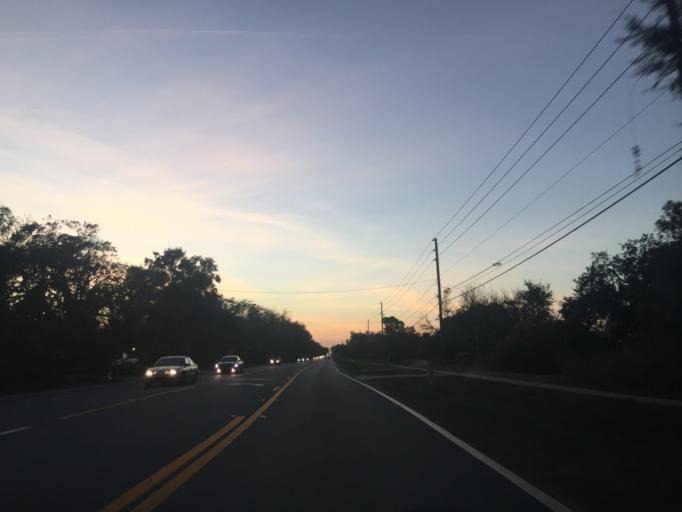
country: US
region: Florida
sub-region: Seminole County
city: Oviedo
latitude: 28.6703
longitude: -81.1958
